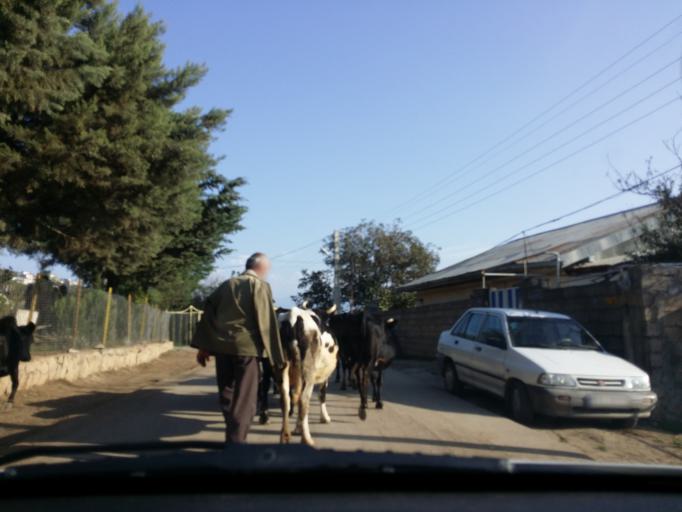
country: IR
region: Mazandaran
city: Chalus
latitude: 36.5417
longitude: 51.2345
